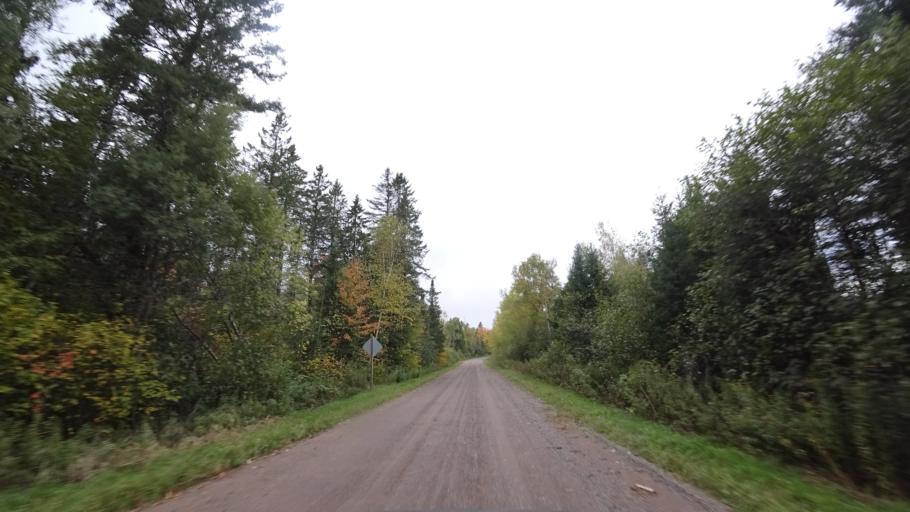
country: US
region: Wisconsin
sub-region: Sawyer County
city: Little Round Lake
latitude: 45.9776
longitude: -90.9934
